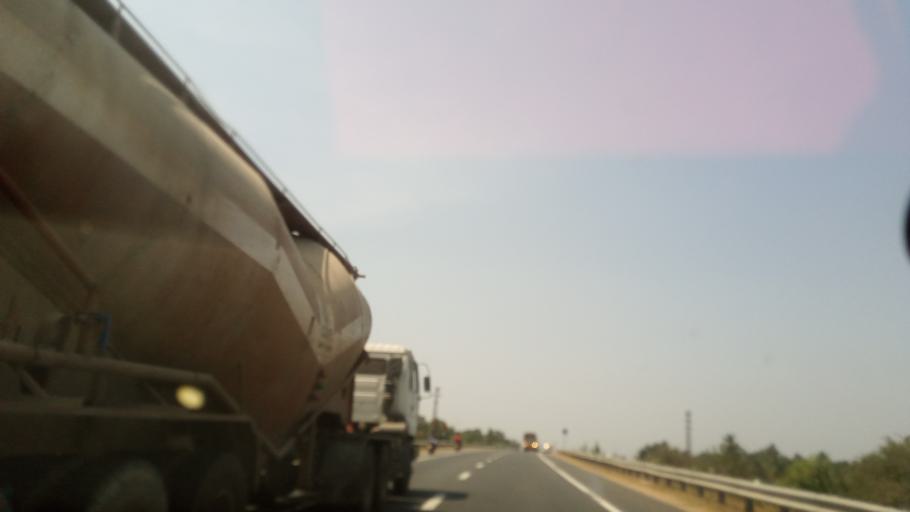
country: IN
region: Tamil Nadu
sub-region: Salem
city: Salem
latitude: 11.6604
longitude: 78.2159
